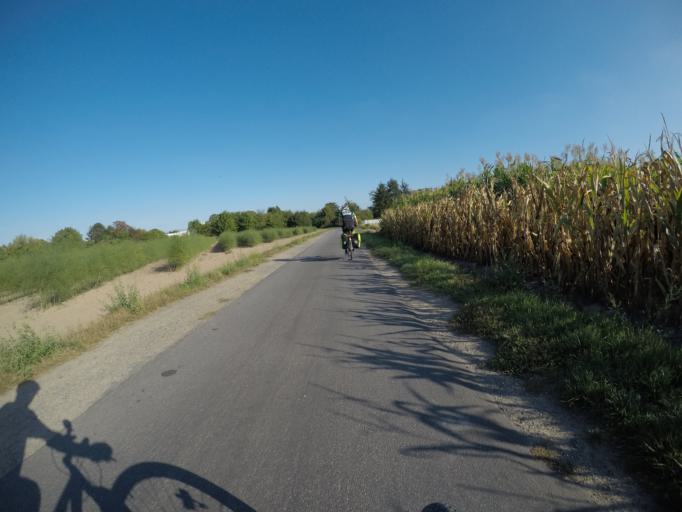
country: DE
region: Hesse
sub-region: Regierungsbezirk Darmstadt
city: Erzhausen
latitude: 49.9190
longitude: 8.6497
